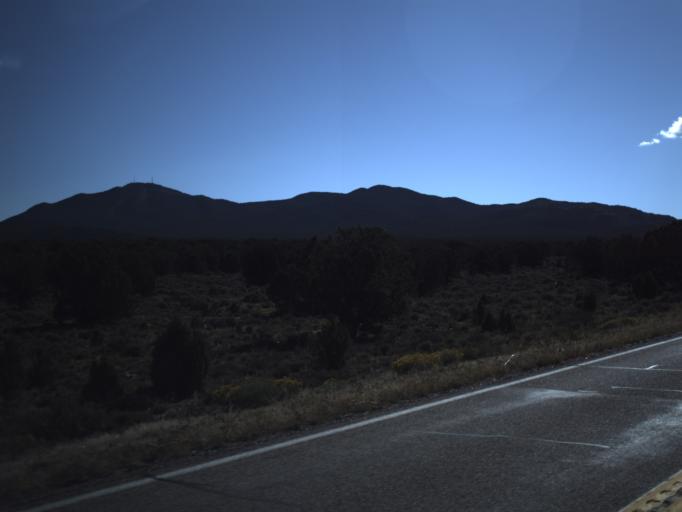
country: US
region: Utah
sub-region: Washington County
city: Enterprise
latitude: 37.6427
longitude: -113.4404
